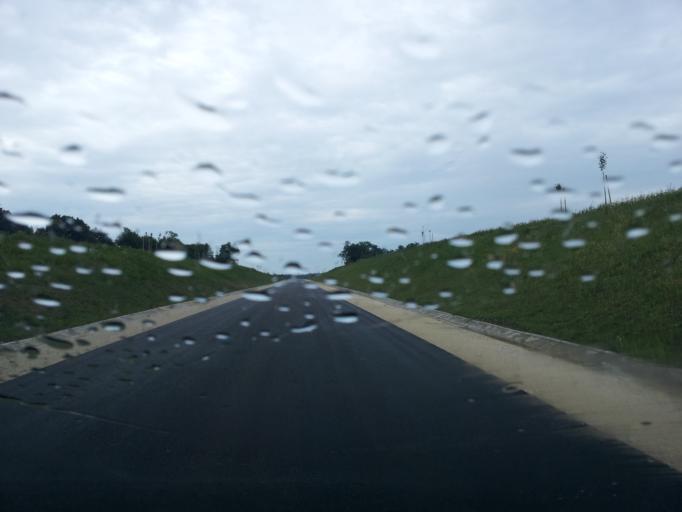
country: HU
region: Vas
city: Kormend
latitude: 46.9598
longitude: 16.6302
